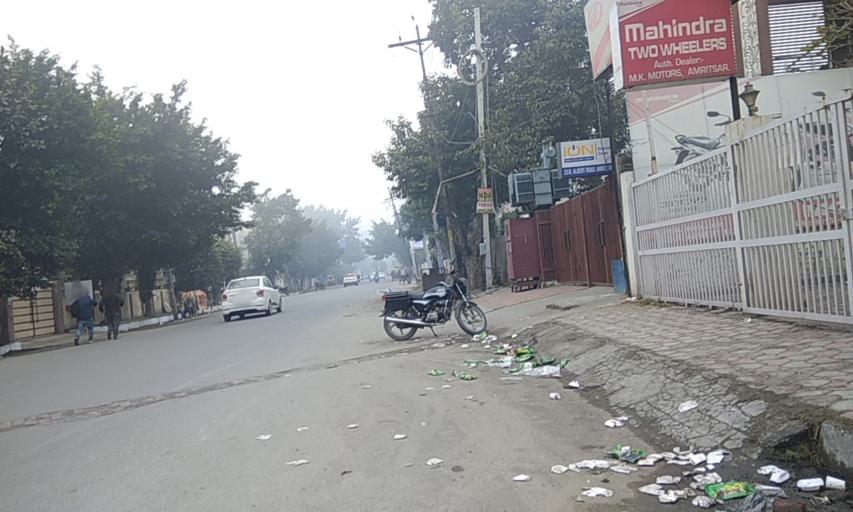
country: IN
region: Punjab
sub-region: Amritsar
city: Amritsar
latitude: 31.6404
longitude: 74.8666
